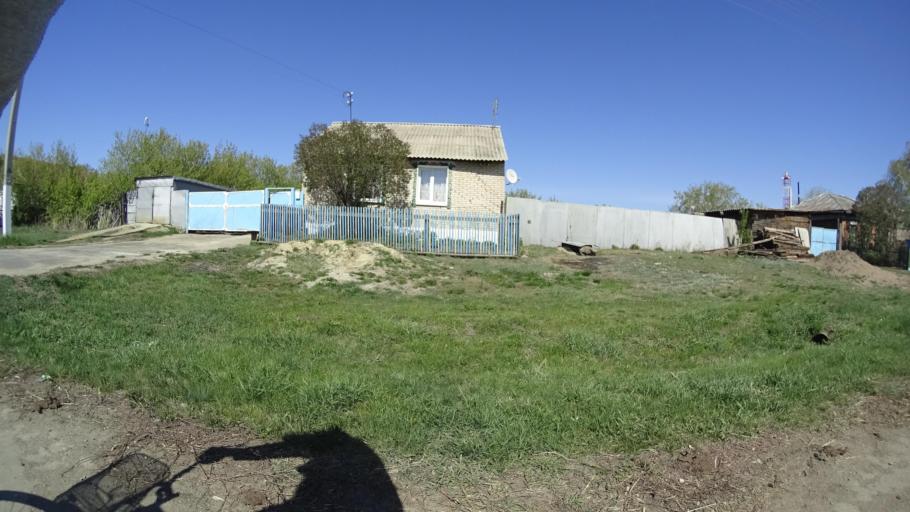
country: RU
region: Chelyabinsk
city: Chesma
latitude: 53.7931
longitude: 61.0365
